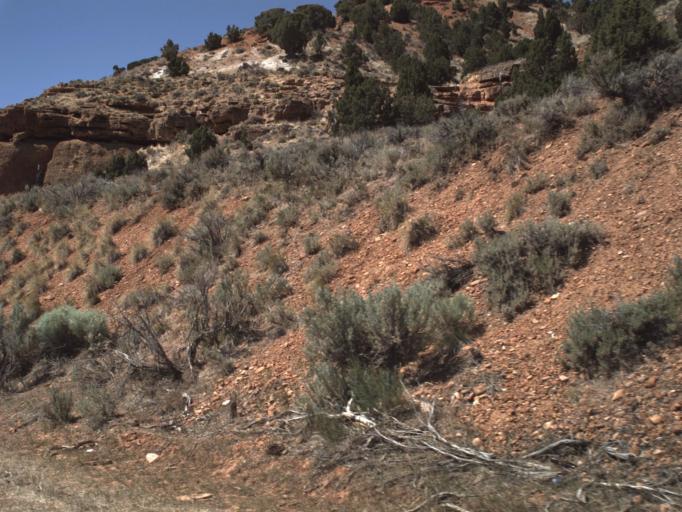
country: US
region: Utah
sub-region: Rich County
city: Randolph
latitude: 41.4980
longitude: -111.2713
